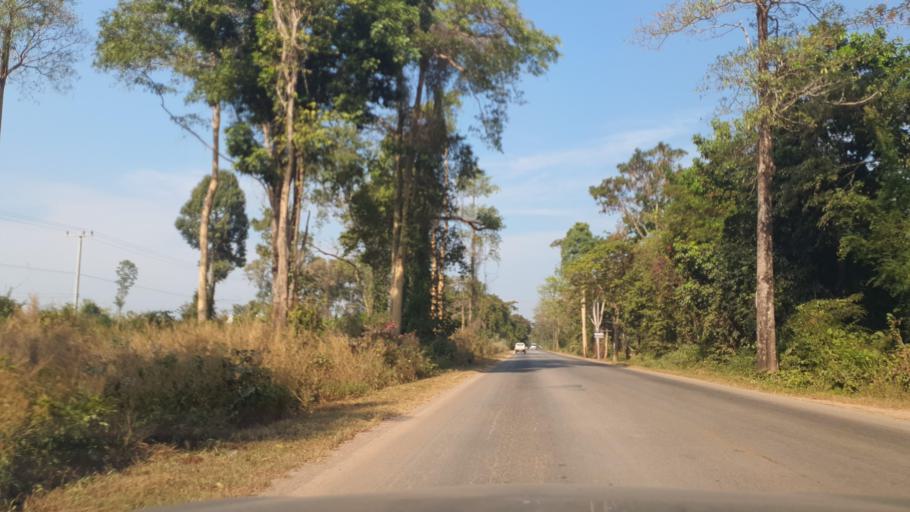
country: TH
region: Nakhon Phanom
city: Ban Phaeng
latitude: 18.0123
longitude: 104.1586
